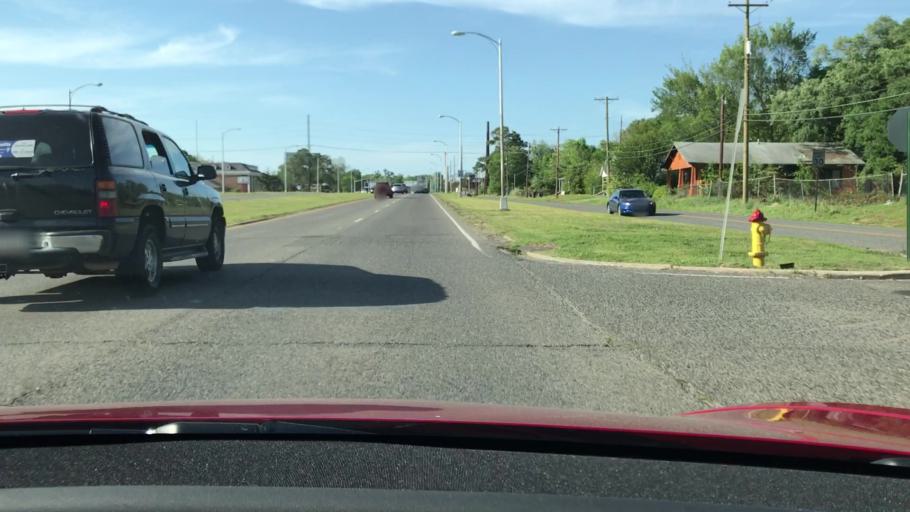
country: US
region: Louisiana
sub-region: Bossier Parish
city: Bossier City
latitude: 32.4964
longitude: -93.7247
